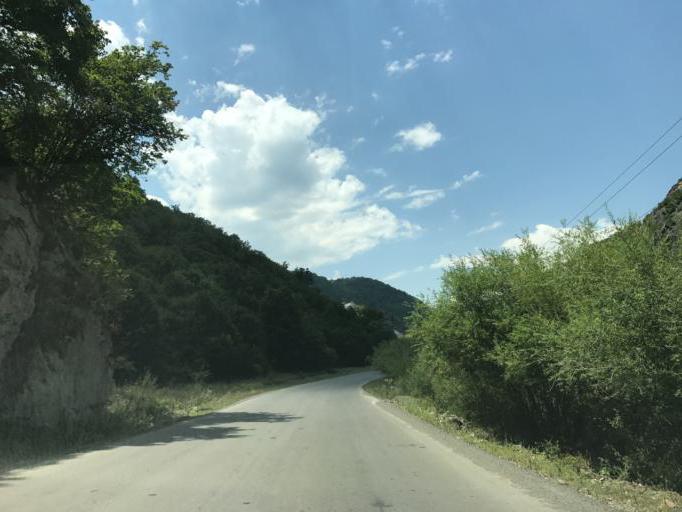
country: AZ
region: Kalbacar Rayonu
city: Kerbakhiar
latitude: 40.2275
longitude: 46.1383
